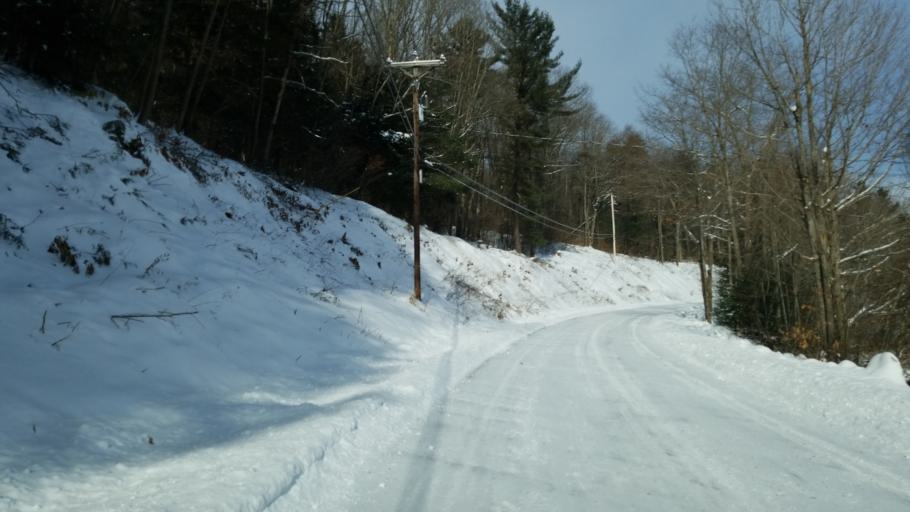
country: US
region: Pennsylvania
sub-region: Clearfield County
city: Clearfield
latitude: 41.0531
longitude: -78.4736
